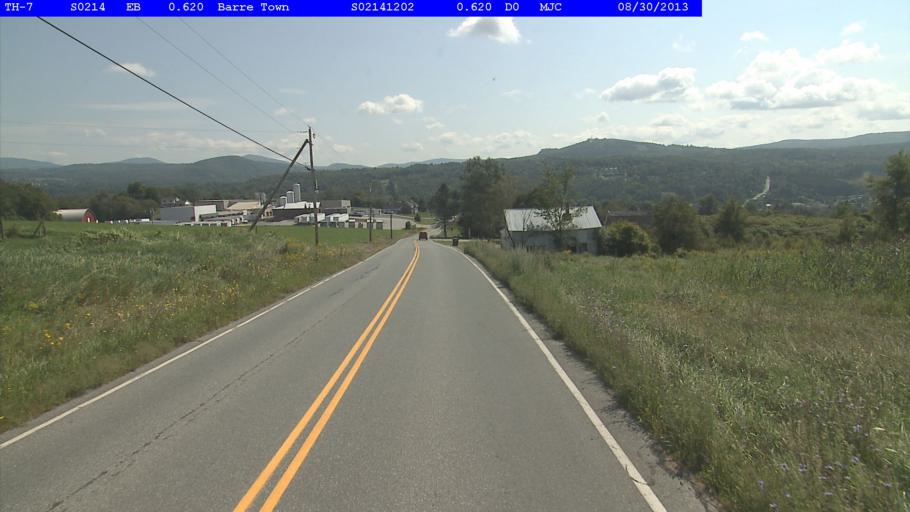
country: US
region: Vermont
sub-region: Washington County
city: South Barre
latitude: 44.1828
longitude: -72.5165
